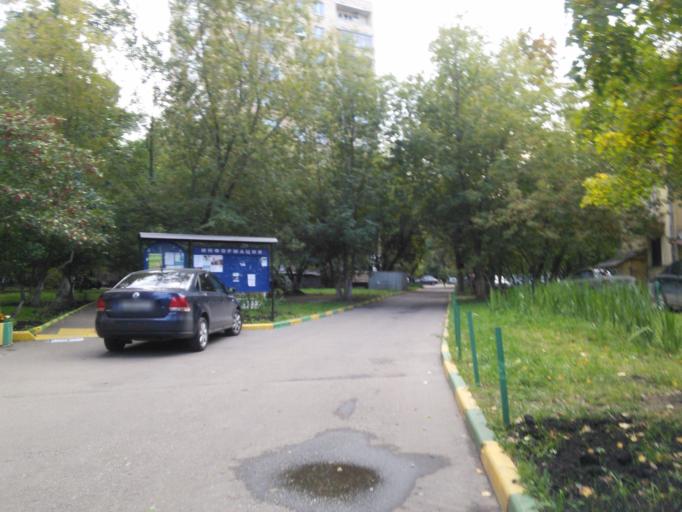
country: RU
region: Moskovskaya
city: Leninskiye Gory
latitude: 55.6964
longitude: 37.5714
